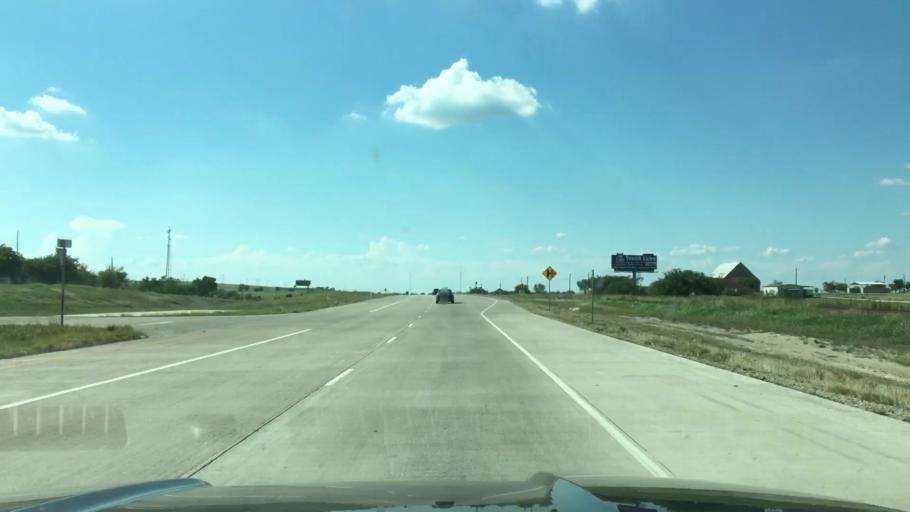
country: US
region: Texas
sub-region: Wise County
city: New Fairview
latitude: 33.1492
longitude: -97.5058
